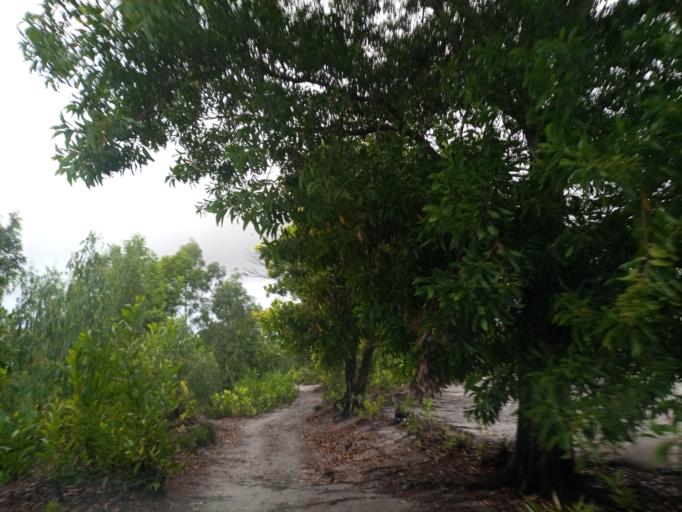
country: MG
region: Anosy
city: Fort Dauphin
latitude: -24.6474
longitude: 47.2043
